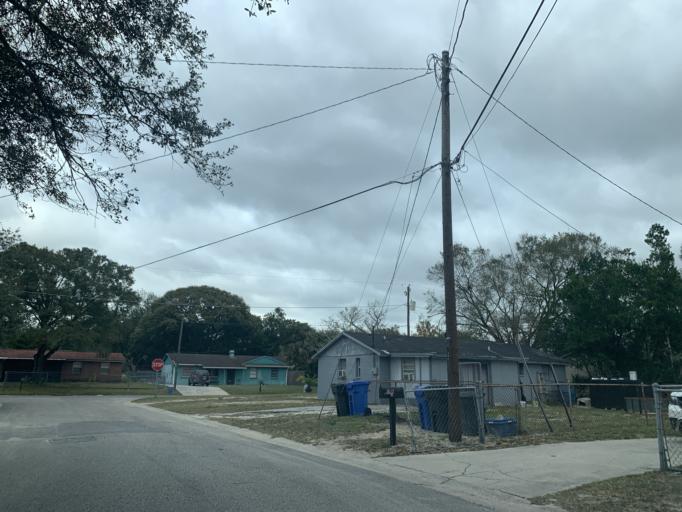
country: US
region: Florida
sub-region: Hillsborough County
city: East Lake-Orient Park
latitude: 27.9766
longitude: -82.3918
